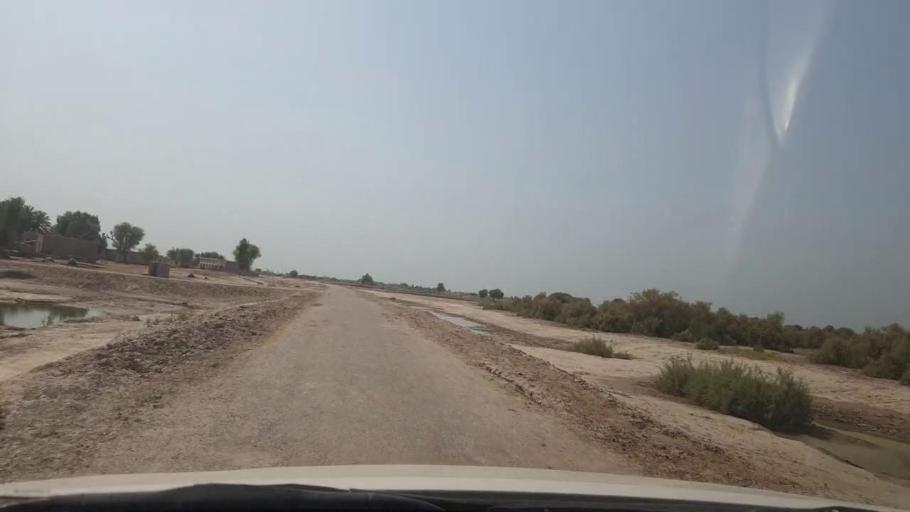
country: PK
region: Sindh
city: Shikarpur
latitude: 28.0080
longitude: 68.7096
